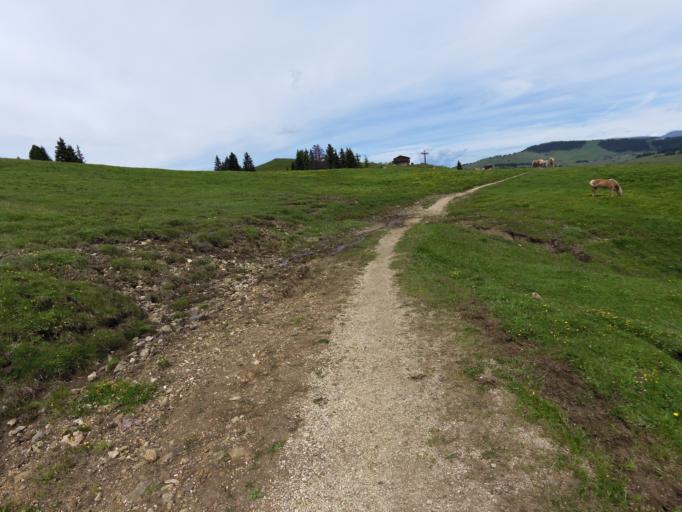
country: IT
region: Trentino-Alto Adige
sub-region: Bolzano
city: Ortisei
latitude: 46.5246
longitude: 11.6516
